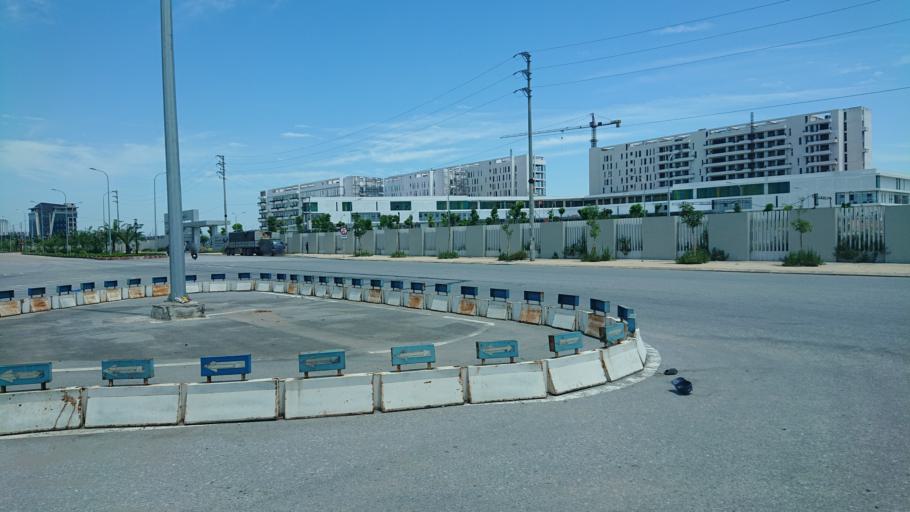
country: VN
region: Ha Nam
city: Thanh Pho Phu Ly
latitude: 20.5391
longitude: 105.9453
